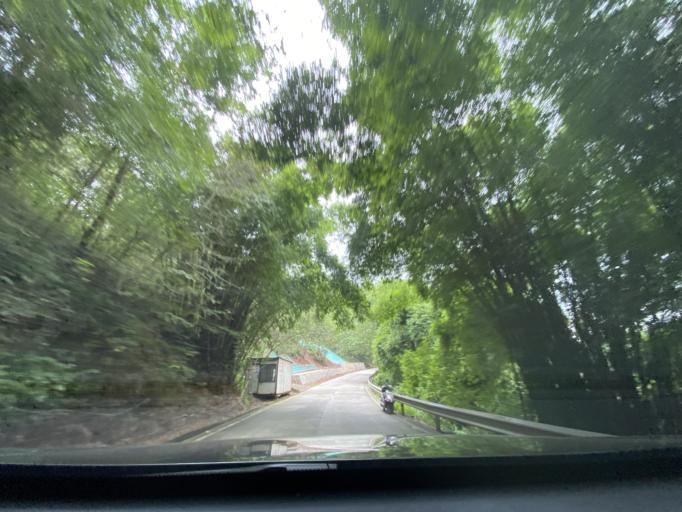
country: CN
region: Sichuan
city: Dongsheng
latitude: 30.4062
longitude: 104.0056
